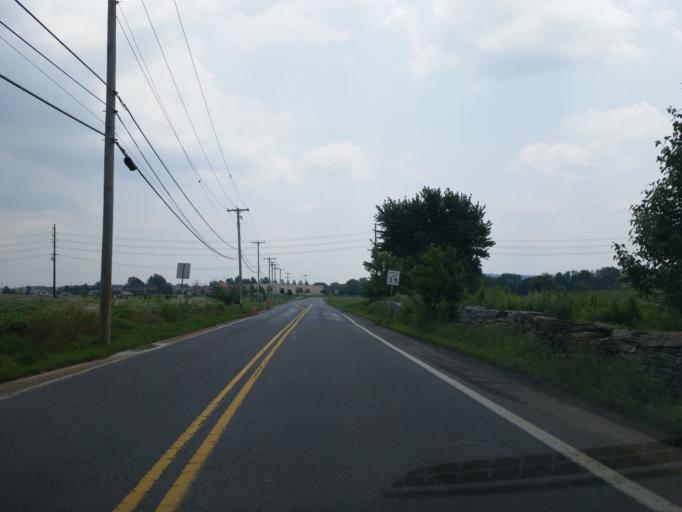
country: US
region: Pennsylvania
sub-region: Lebanon County
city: Campbelltown
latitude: 40.2857
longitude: -76.5954
